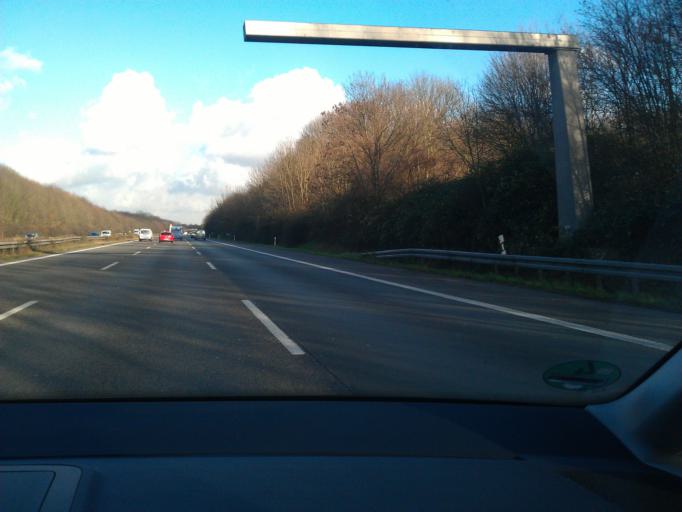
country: DE
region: North Rhine-Westphalia
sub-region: Regierungsbezirk Koln
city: Bilderstoeckchen
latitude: 51.0086
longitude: 6.9124
